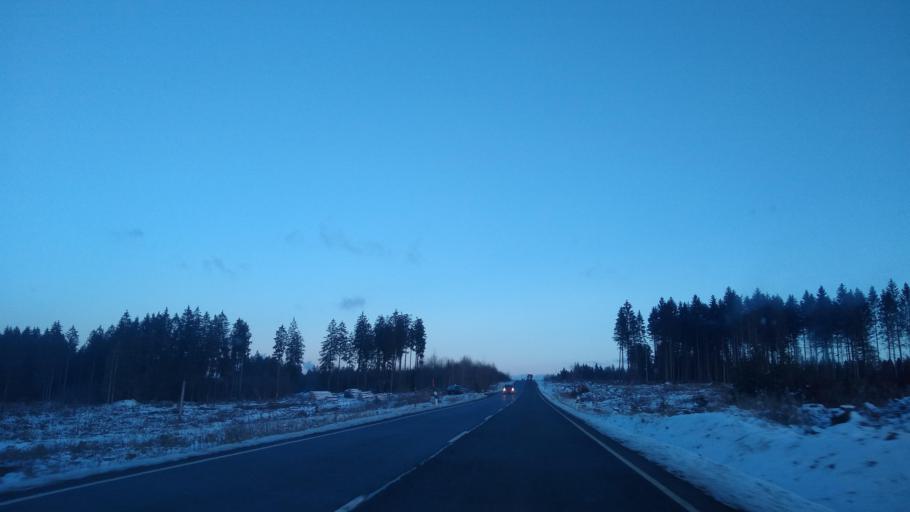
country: DE
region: Lower Saxony
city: Clausthal-Zellerfeld
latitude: 51.7902
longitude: 10.3727
